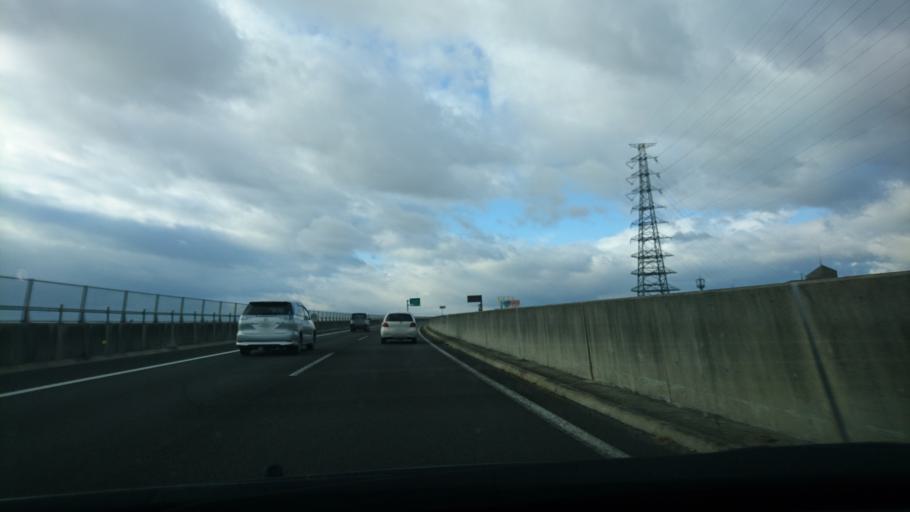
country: JP
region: Miyagi
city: Rifu
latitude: 38.2770
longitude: 140.9898
